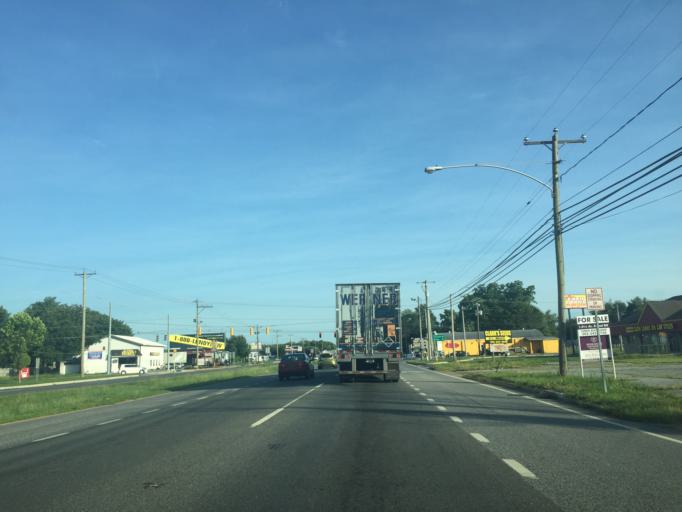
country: US
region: Delaware
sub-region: Kent County
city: Cheswold
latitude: 39.2245
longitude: -75.5771
